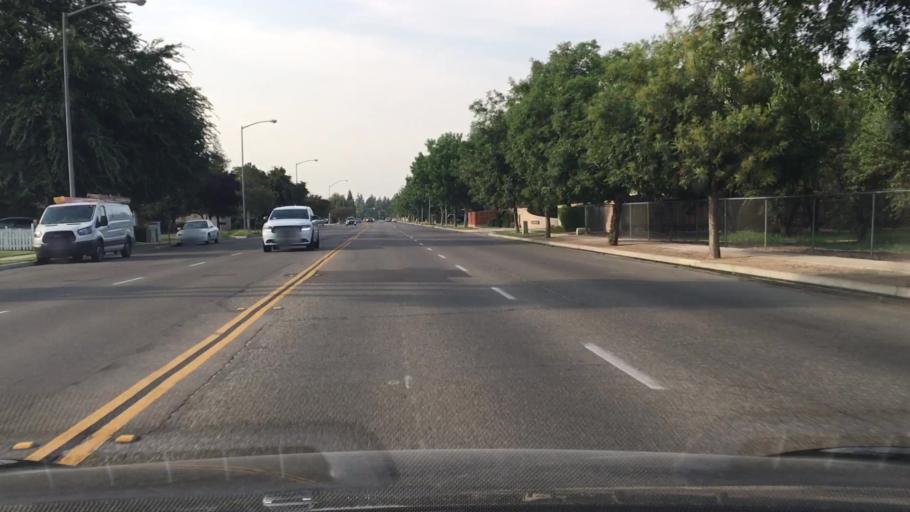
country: US
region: California
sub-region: Fresno County
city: Clovis
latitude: 36.8330
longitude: -119.7361
